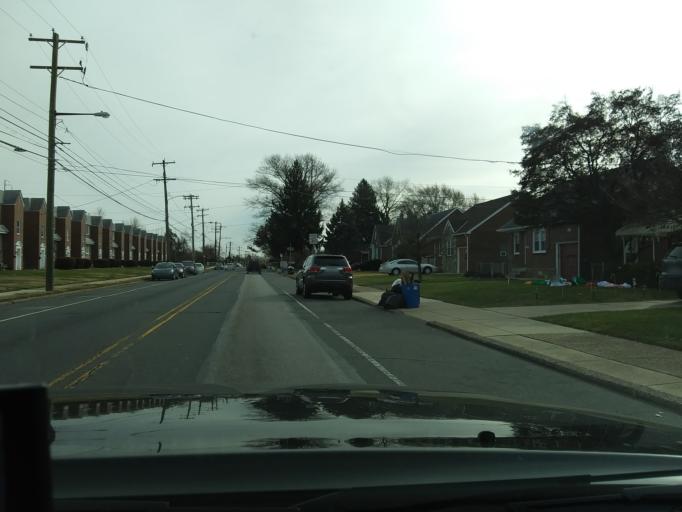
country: US
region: Pennsylvania
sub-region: Montgomery County
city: Rockledge
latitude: 40.0700
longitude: -75.0700
